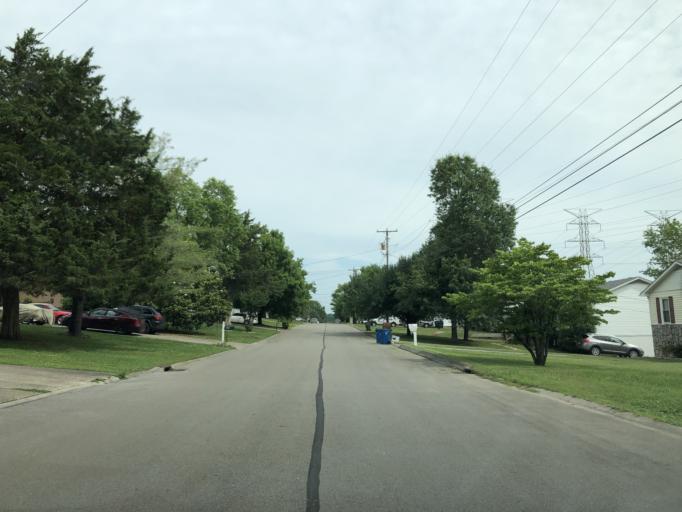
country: US
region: Tennessee
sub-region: Davidson County
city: Goodlettsville
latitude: 36.2822
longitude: -86.7161
